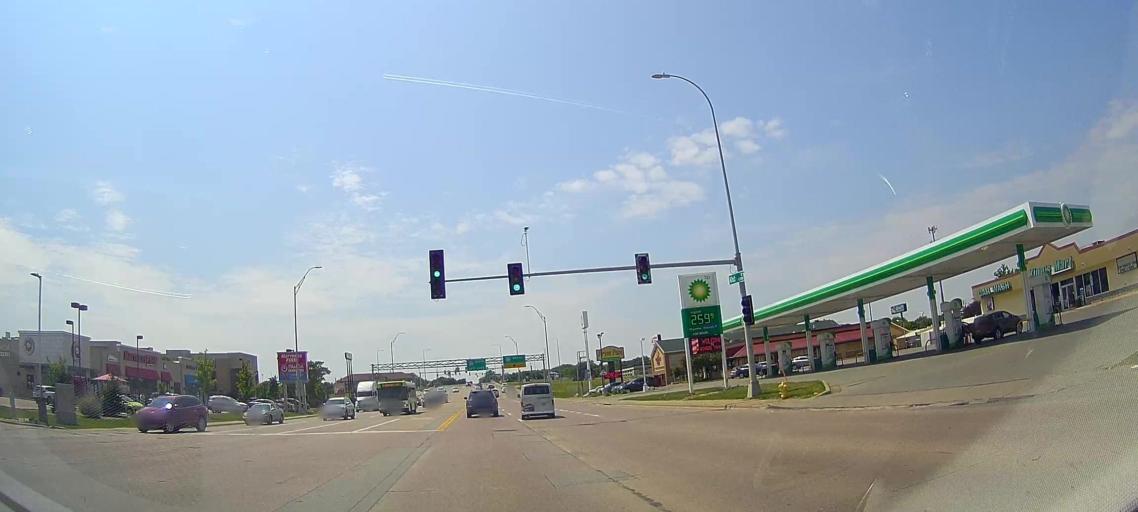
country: US
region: South Dakota
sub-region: Minnehaha County
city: Sioux Falls
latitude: 43.5149
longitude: -96.7766
